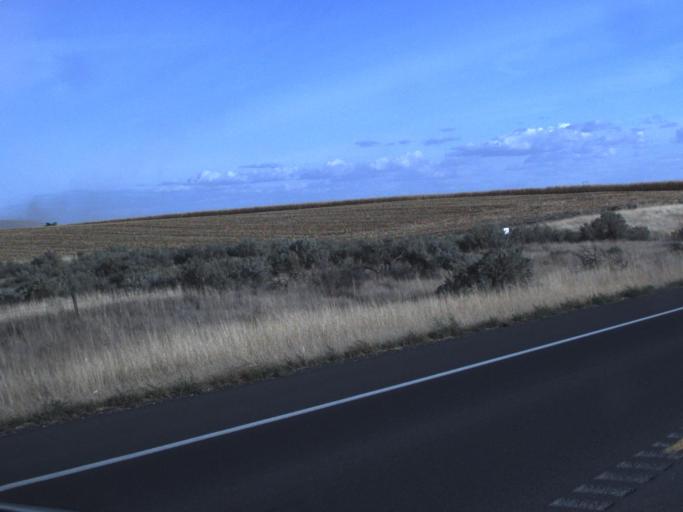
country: US
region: Oregon
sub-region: Umatilla County
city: Umatilla
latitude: 45.9539
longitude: -119.4052
